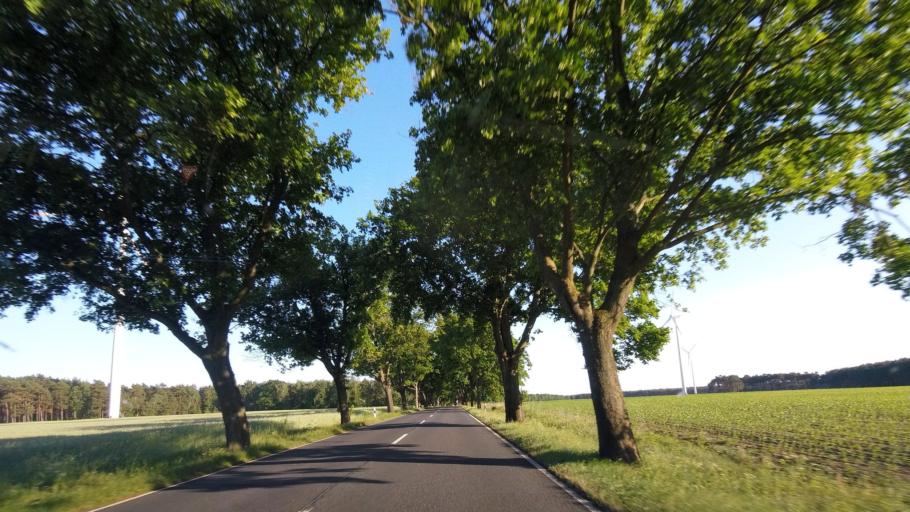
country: DE
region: Brandenburg
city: Golzow
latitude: 52.3158
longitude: 12.6082
